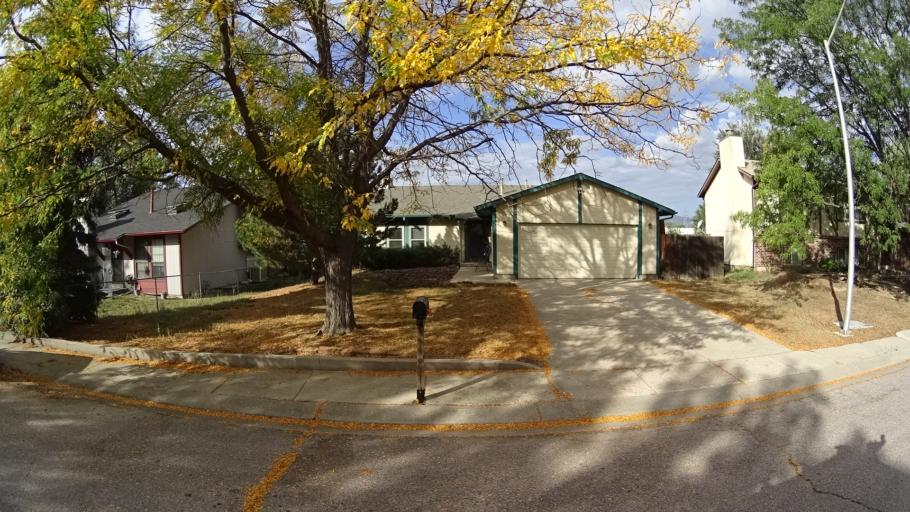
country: US
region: Colorado
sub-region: El Paso County
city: Cimarron Hills
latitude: 38.8574
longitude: -104.7524
